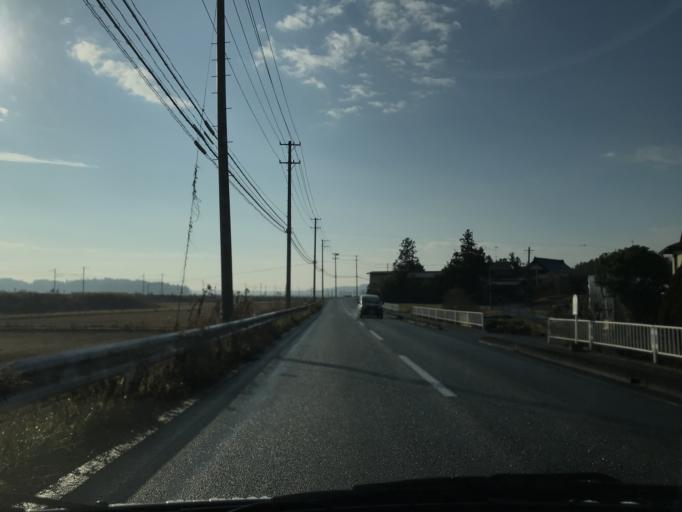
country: JP
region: Iwate
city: Ichinoseki
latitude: 38.8052
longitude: 141.1770
